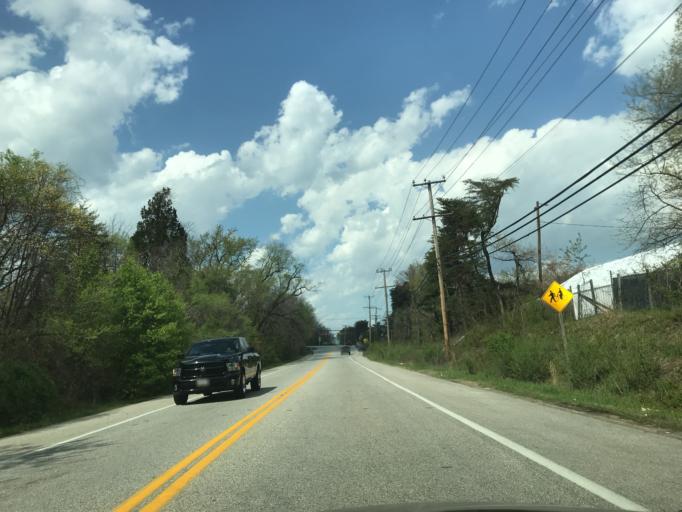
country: US
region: Maryland
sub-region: Anne Arundel County
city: Ferndale
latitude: 39.1604
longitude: -76.6676
